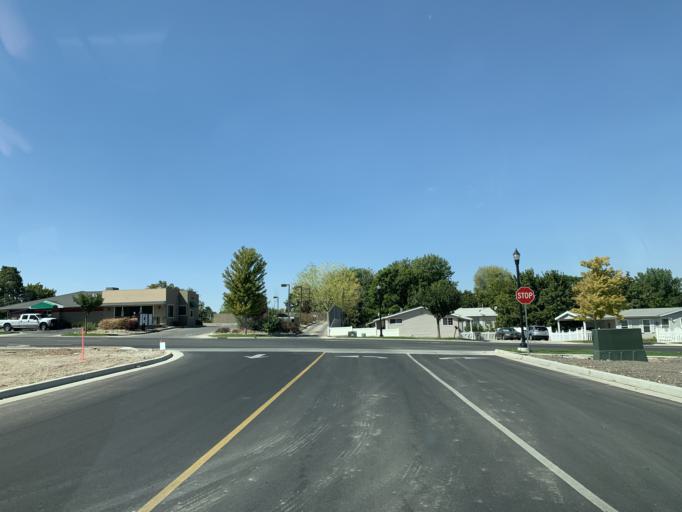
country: US
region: Utah
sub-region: Utah County
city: Santaquin
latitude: 39.9765
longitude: -111.7764
